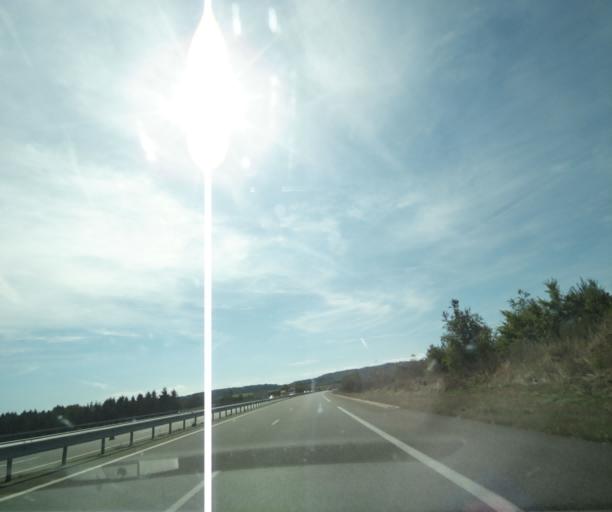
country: FR
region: Auvergne
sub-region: Departement du Puy-de-Dome
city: Chapdes-Beaufort
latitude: 45.8440
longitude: 2.8310
